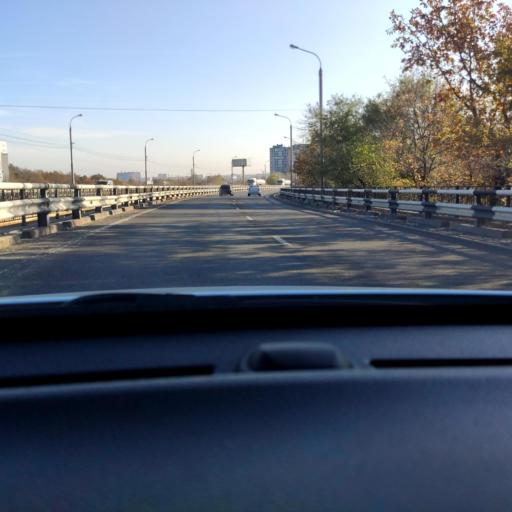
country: RU
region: Voronezj
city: Voronezh
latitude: 51.6960
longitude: 39.2232
